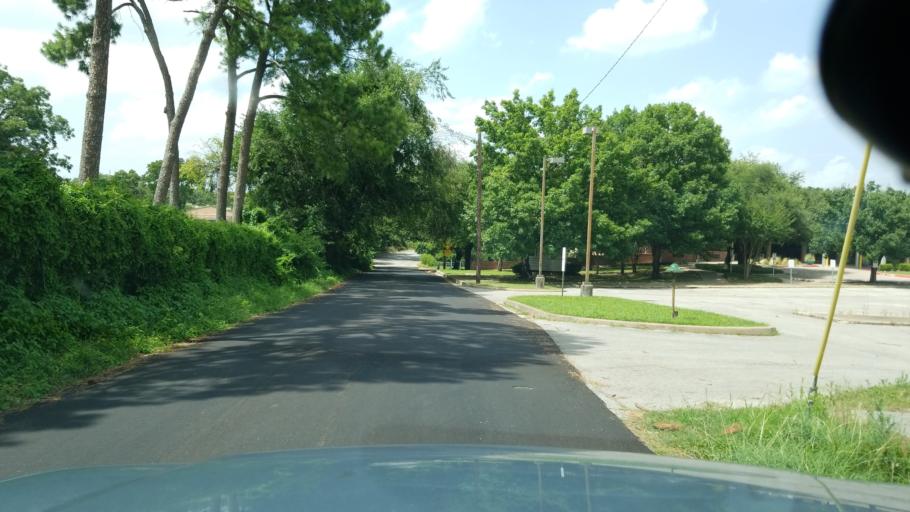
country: US
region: Texas
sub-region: Dallas County
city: University Park
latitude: 32.8317
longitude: -96.8625
